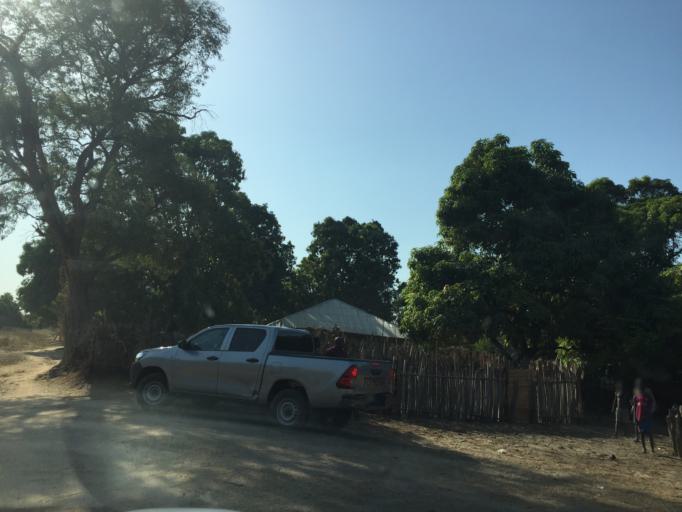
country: GW
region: Oio
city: Farim
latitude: 12.4603
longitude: -15.3031
